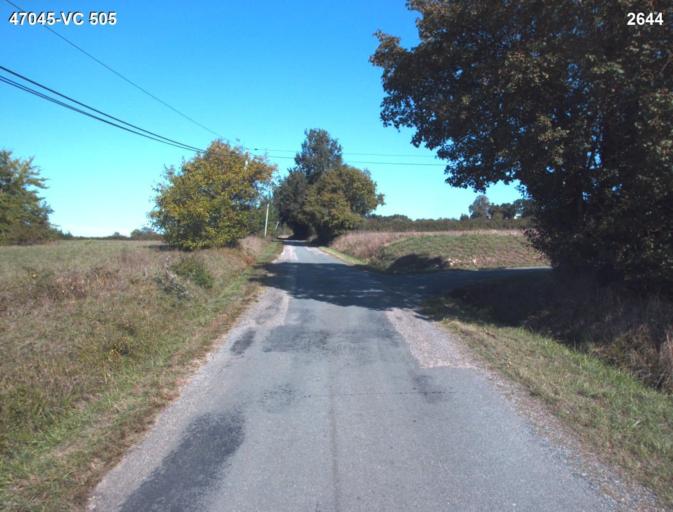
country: FR
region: Aquitaine
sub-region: Departement du Lot-et-Garonne
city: Nerac
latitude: 44.1413
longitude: 0.4164
